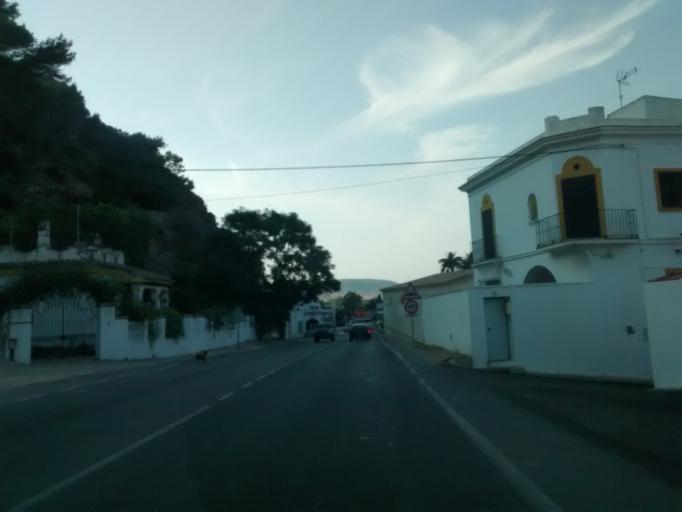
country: ES
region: Andalusia
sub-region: Provincia de Cadiz
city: Vejer de la Frontera
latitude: 36.2524
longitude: -5.9561
